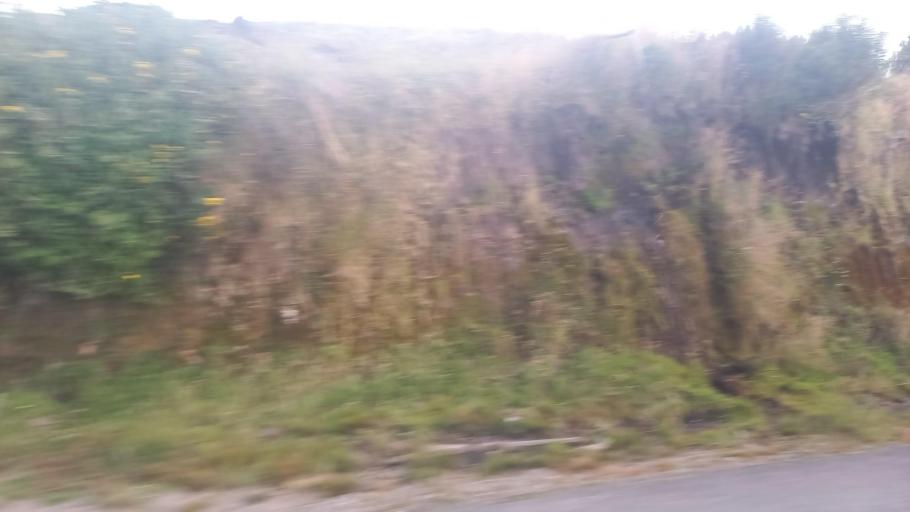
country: EC
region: Pichincha
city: Cayambe
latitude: 0.1026
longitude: -78.0834
